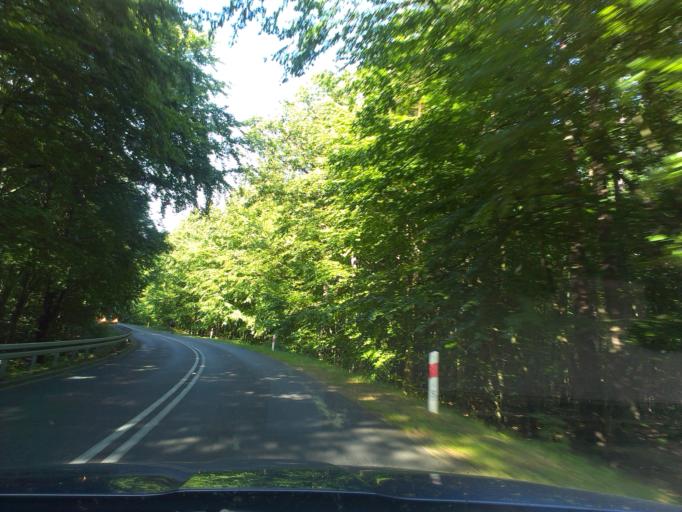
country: PL
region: West Pomeranian Voivodeship
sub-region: Powiat kamienski
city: Miedzyzdroje
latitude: 53.9438
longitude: 14.4865
